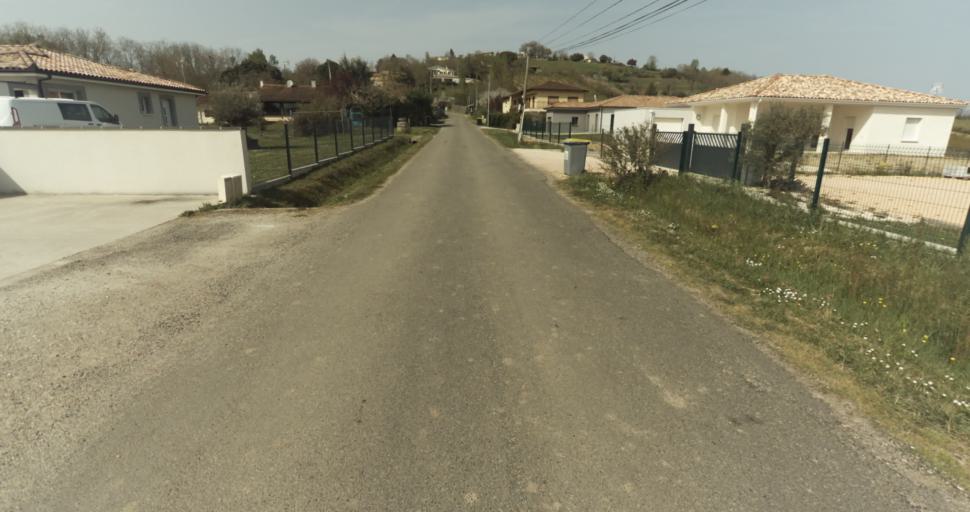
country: FR
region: Midi-Pyrenees
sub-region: Departement du Tarn-et-Garonne
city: Moissac
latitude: 44.1280
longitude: 1.1497
